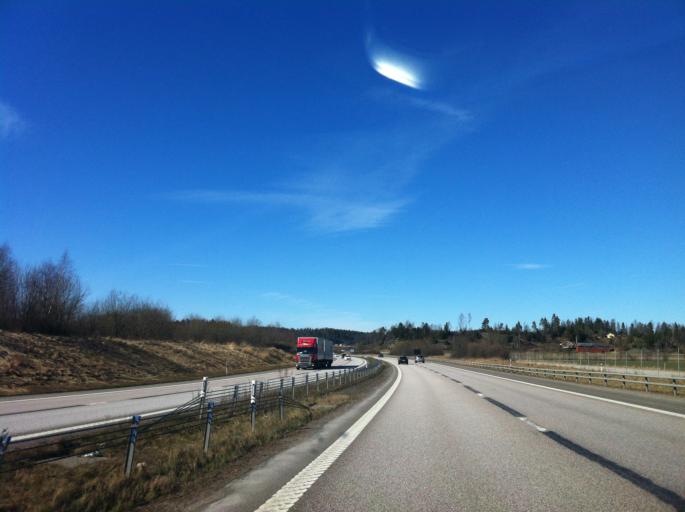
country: SE
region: Vaestra Goetaland
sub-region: Uddevalla Kommun
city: Uddevalla
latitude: 58.3560
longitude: 11.8155
